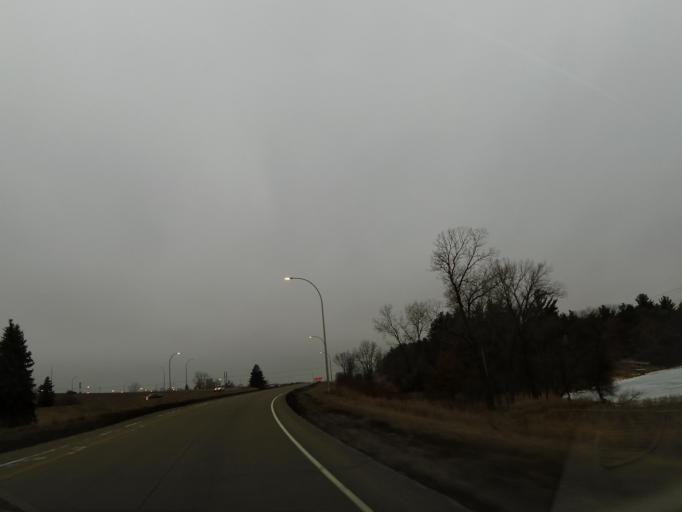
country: US
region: Minnesota
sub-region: Washington County
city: Birchwood
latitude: 45.0309
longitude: -92.9596
